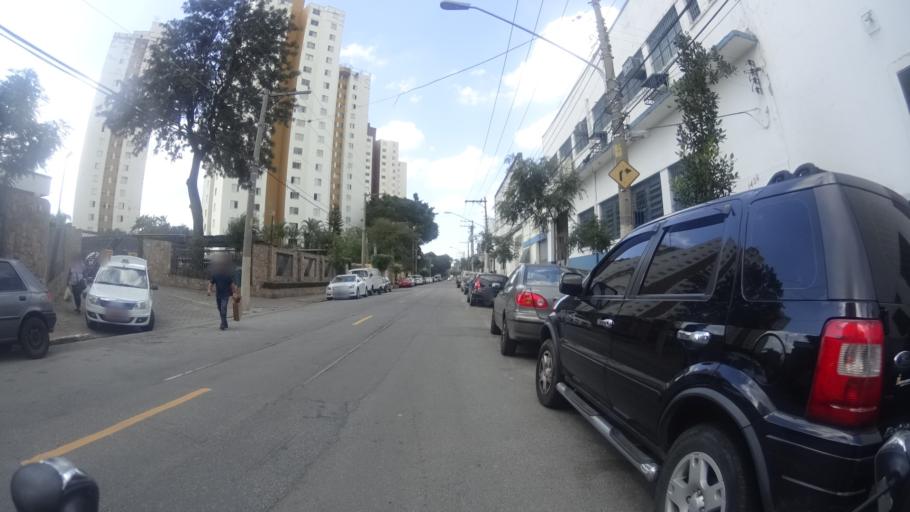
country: BR
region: Sao Paulo
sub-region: Sao Paulo
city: Sao Paulo
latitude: -23.5487
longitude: -46.6122
